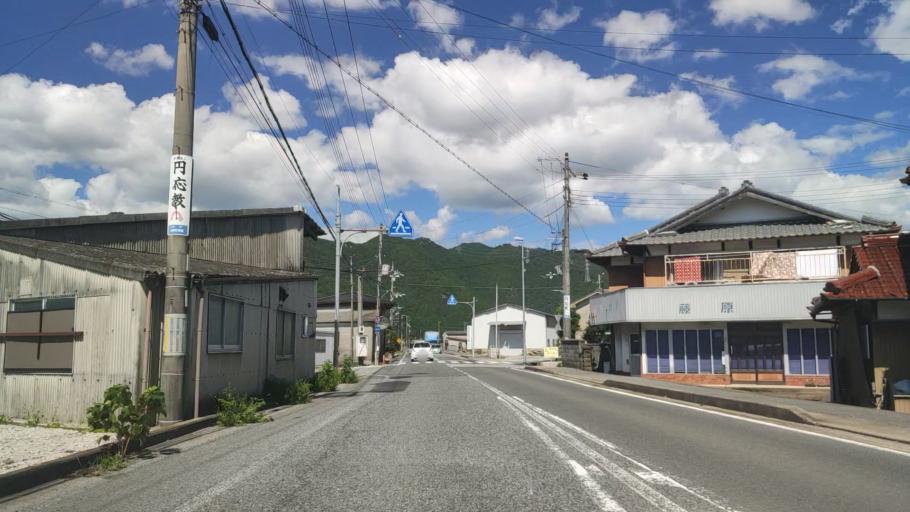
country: JP
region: Hyogo
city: Nishiwaki
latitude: 35.1018
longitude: 134.9957
